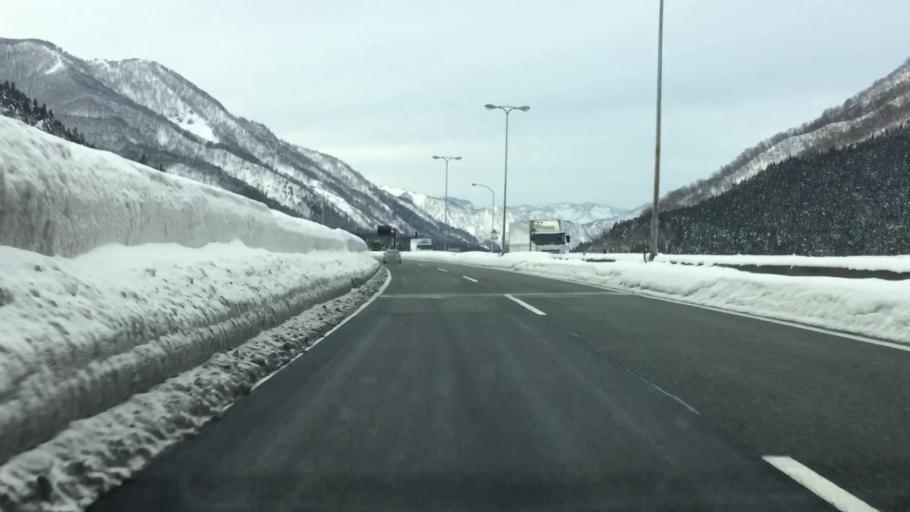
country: JP
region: Niigata
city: Shiozawa
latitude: 36.8746
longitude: 138.8631
